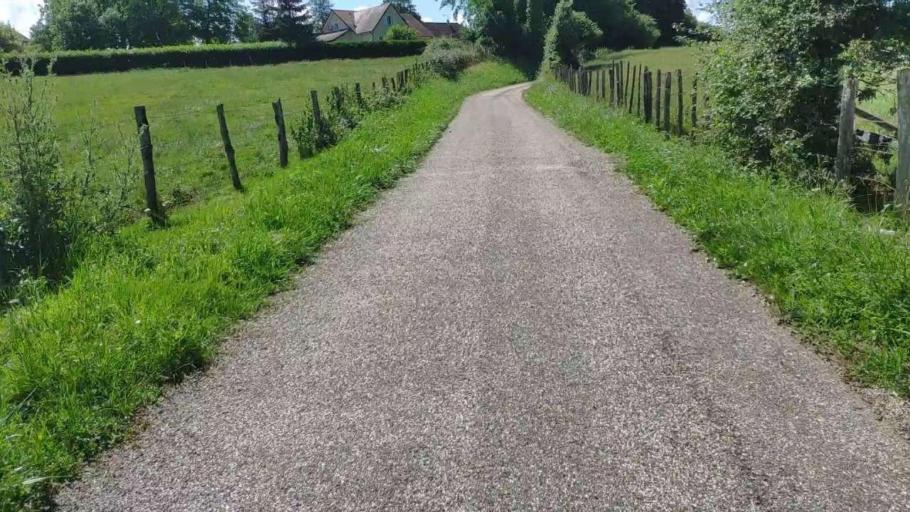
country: FR
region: Franche-Comte
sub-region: Departement du Jura
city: Poligny
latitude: 46.8327
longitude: 5.5651
